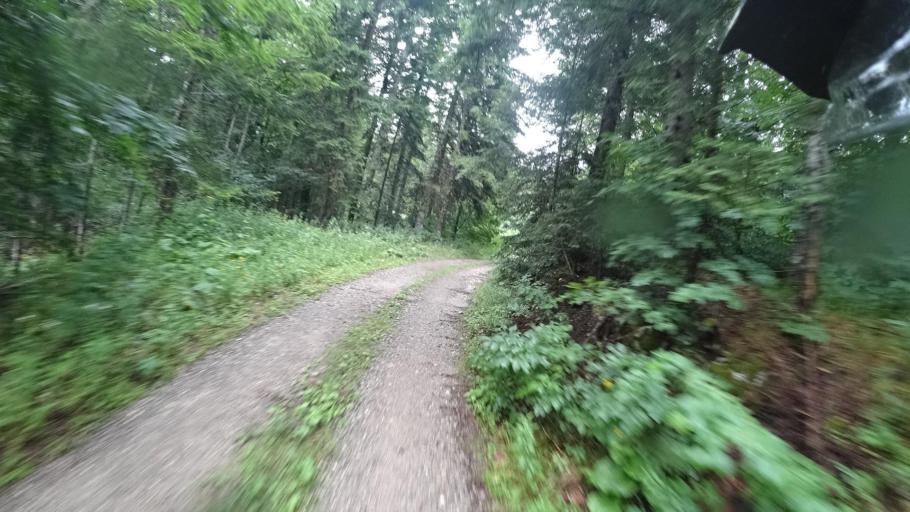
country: HR
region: Karlovacka
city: Plaski
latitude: 44.9308
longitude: 15.4233
